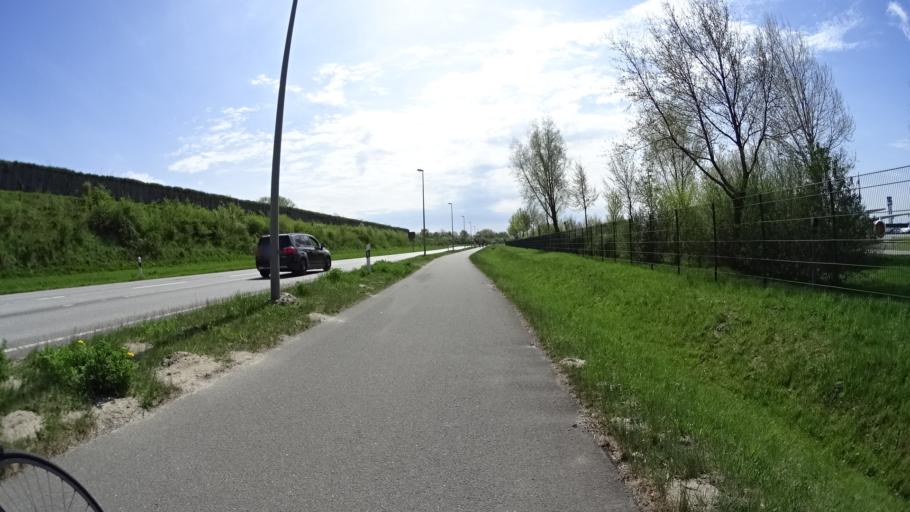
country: DE
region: Lower Saxony
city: Neu Wulmstorf
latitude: 53.5334
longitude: 9.8430
